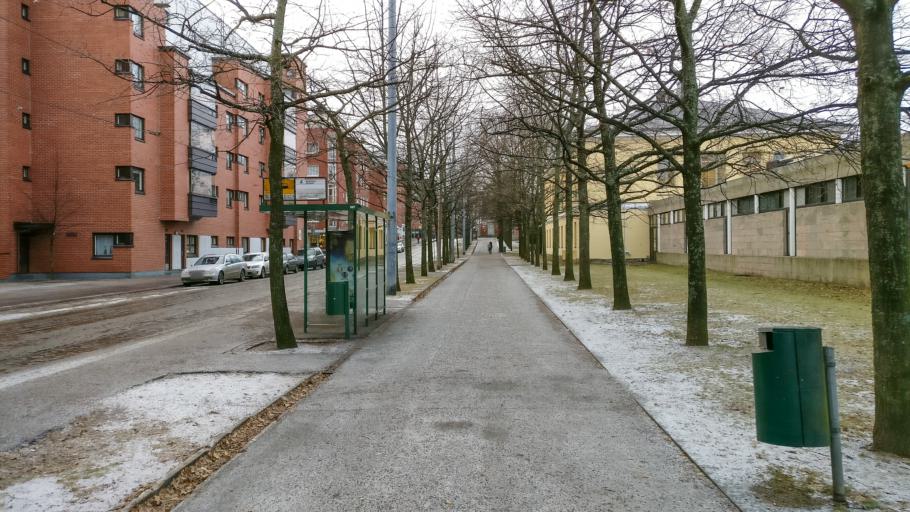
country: FI
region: Uusimaa
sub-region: Helsinki
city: Helsinki
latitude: 60.1674
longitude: 24.9743
